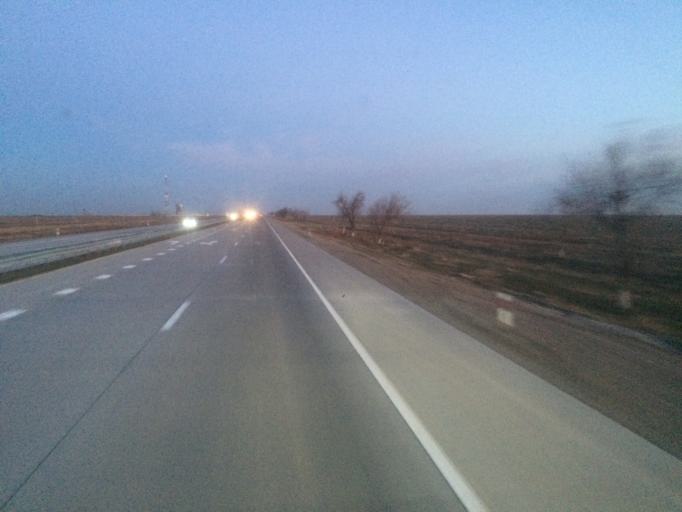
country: KZ
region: Ongtustik Qazaqstan
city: Temirlanovka
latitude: 42.8348
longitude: 69.1184
